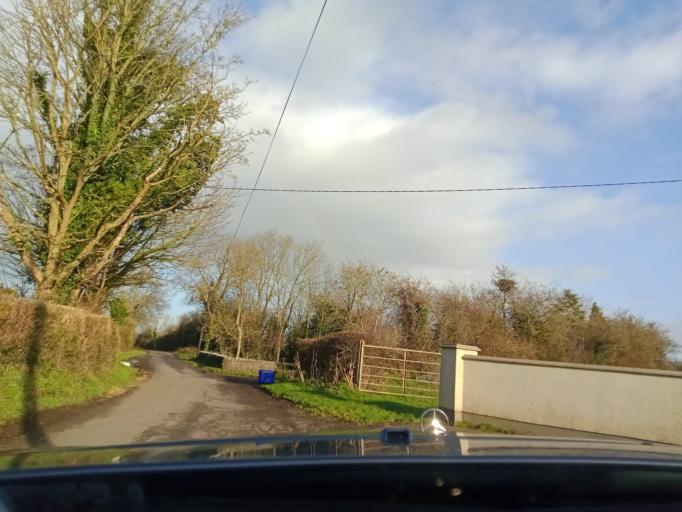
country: IE
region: Leinster
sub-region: Kilkenny
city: Callan
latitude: 52.4942
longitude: -7.3573
